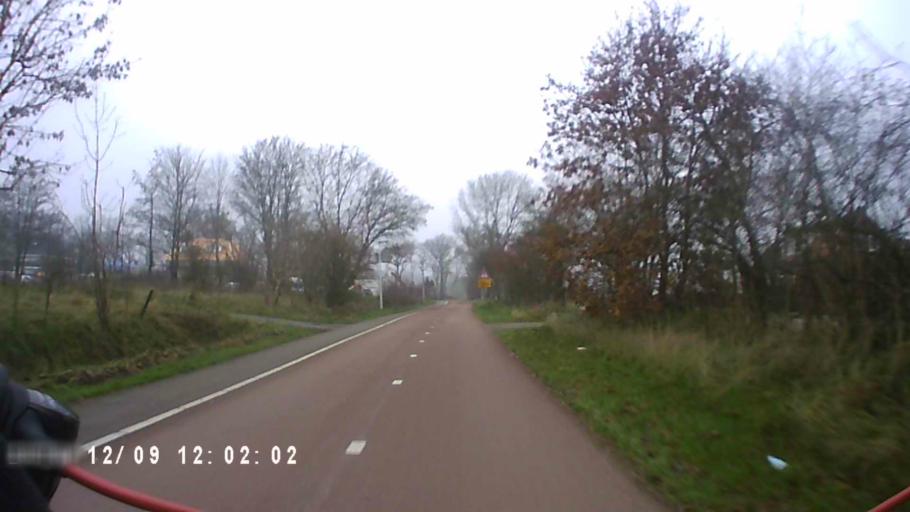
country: NL
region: Groningen
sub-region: Gemeente Haren
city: Haren
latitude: 53.1863
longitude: 6.5995
